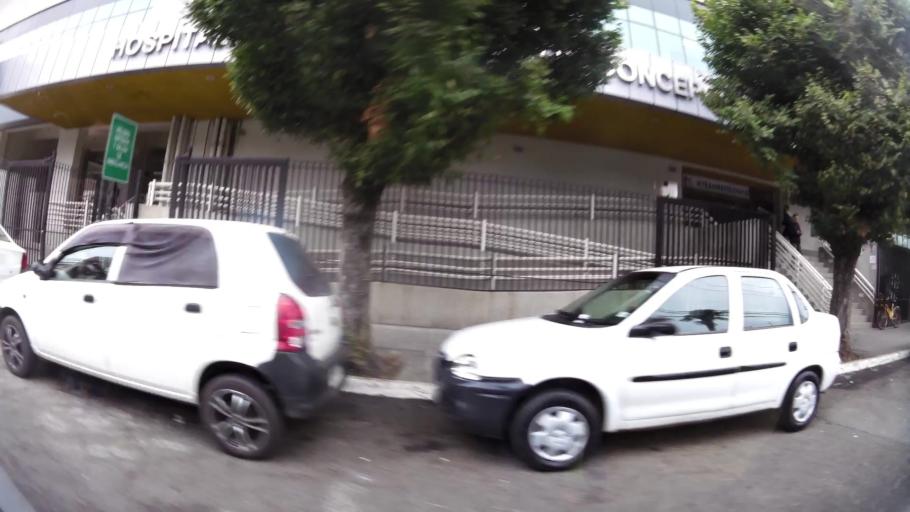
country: CL
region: Biobio
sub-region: Provincia de Concepcion
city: Concepcion
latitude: -36.8239
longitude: -73.0379
